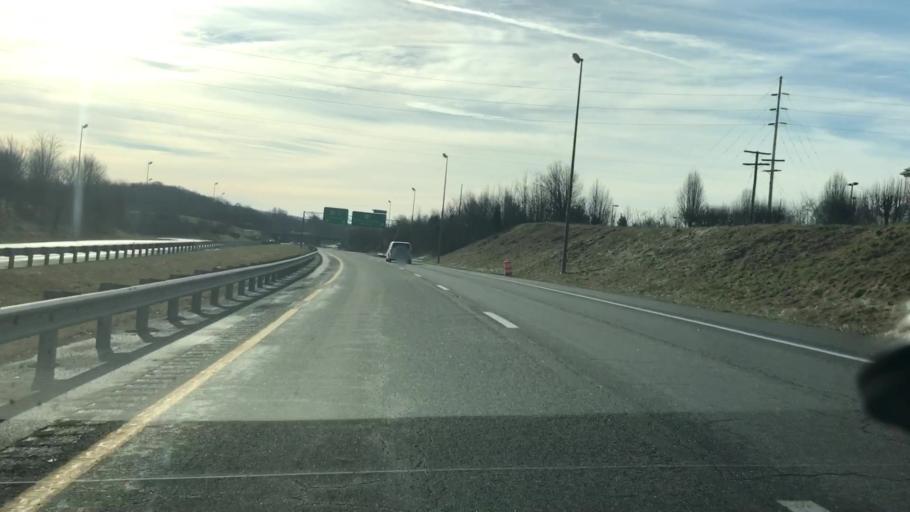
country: US
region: Virginia
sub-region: Montgomery County
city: Merrimac
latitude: 37.1702
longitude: -80.4170
